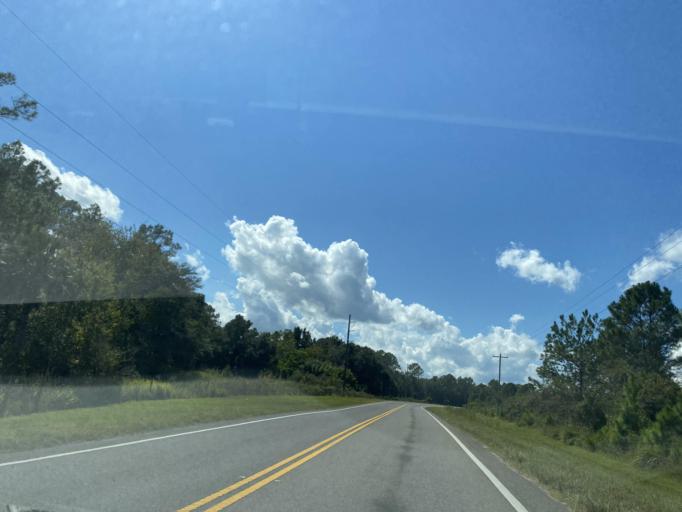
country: US
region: Florida
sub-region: Lake County
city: Umatilla
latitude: 28.9616
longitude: -81.5983
